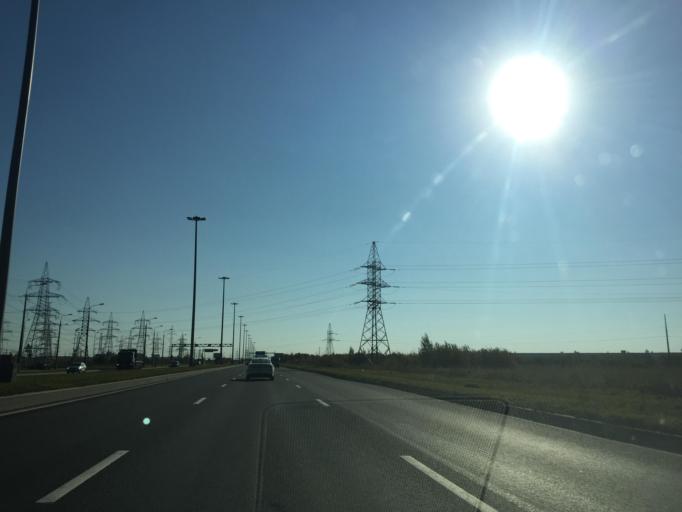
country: RU
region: St.-Petersburg
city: Petro-Slavyanka
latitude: 59.7549
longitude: 30.5206
